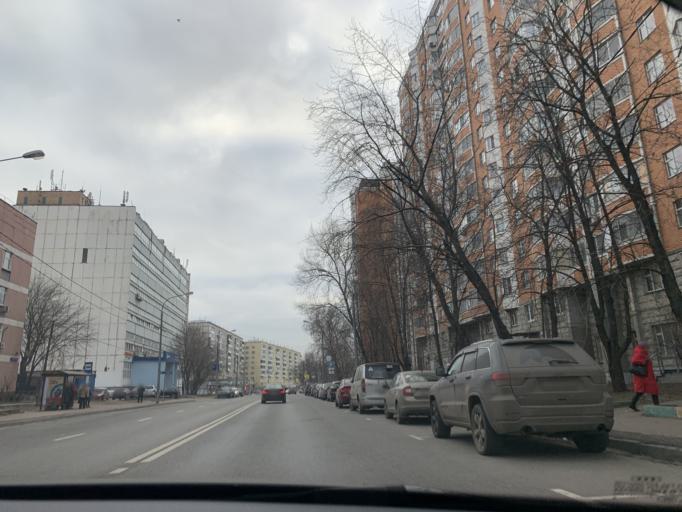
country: RU
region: Moscow
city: Likhobory
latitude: 55.8650
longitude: 37.5654
